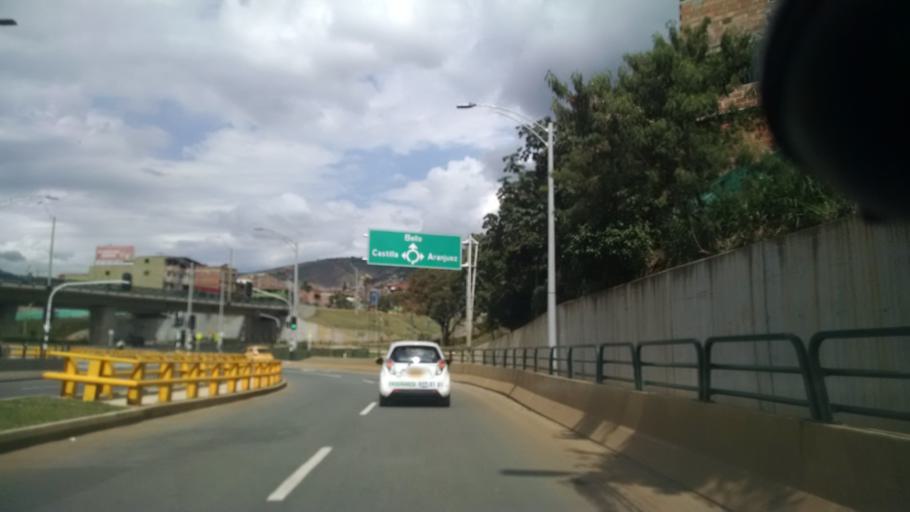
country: CO
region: Antioquia
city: Medellin
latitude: 6.2846
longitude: -75.5649
